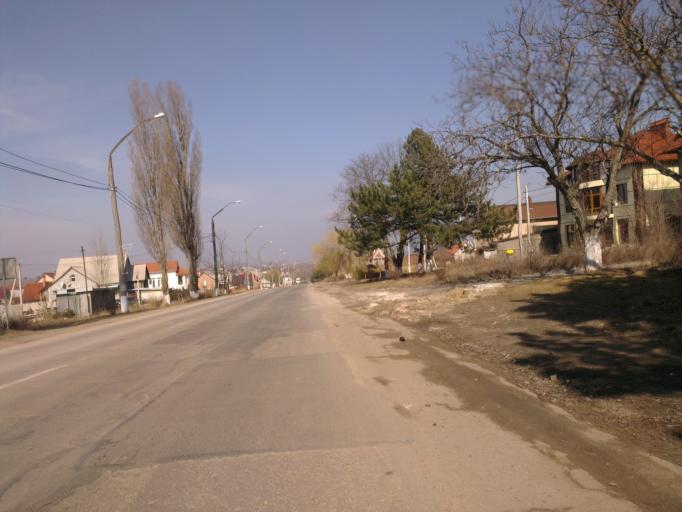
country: MD
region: Chisinau
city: Cricova
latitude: 47.1185
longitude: 28.8677
